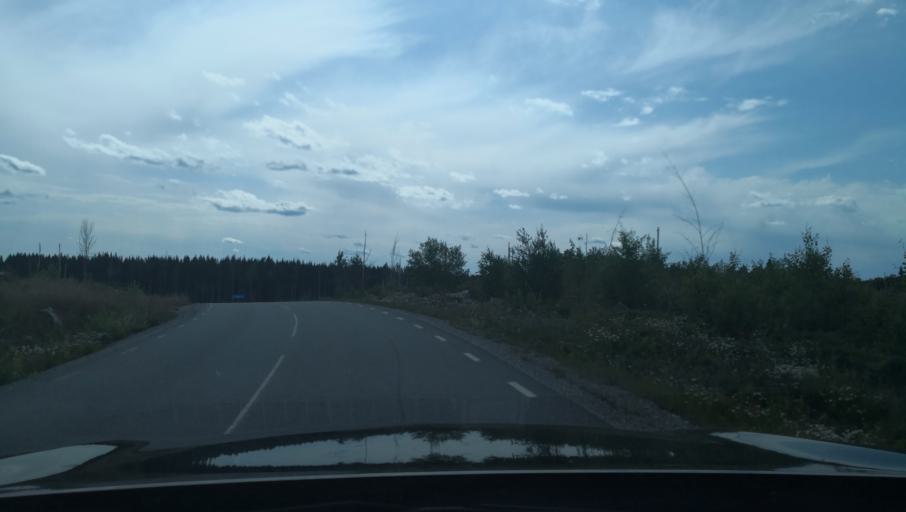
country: SE
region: Vaestmanland
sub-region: Norbergs Kommun
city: Norberg
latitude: 59.9769
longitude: 16.0370
